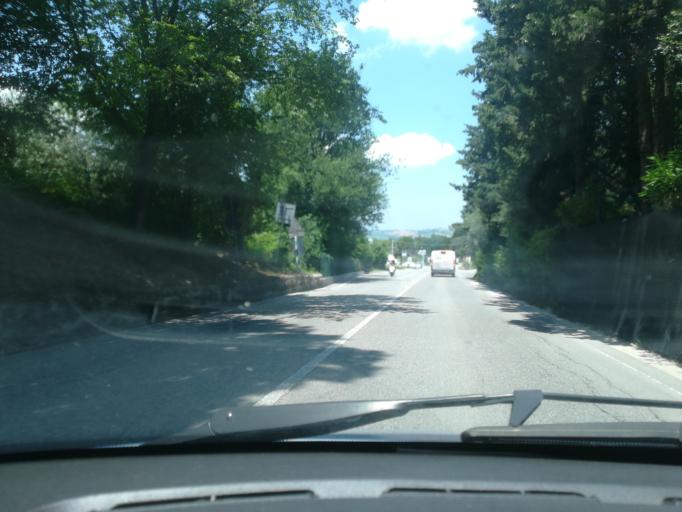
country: IT
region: The Marches
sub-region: Provincia di Macerata
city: Villa Potenza
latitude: 43.3118
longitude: 13.4350
